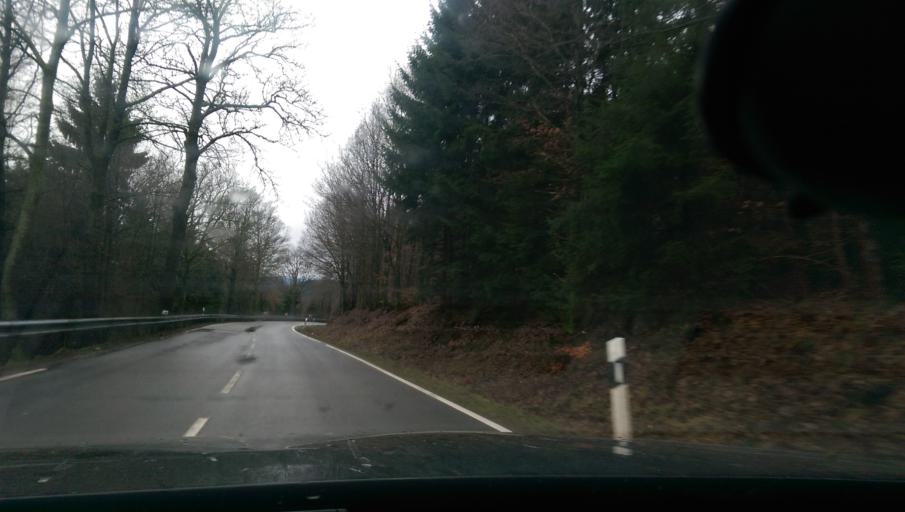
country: DE
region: North Rhine-Westphalia
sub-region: Regierungsbezirk Arnsberg
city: Finnentrop
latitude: 51.2387
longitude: 7.9602
